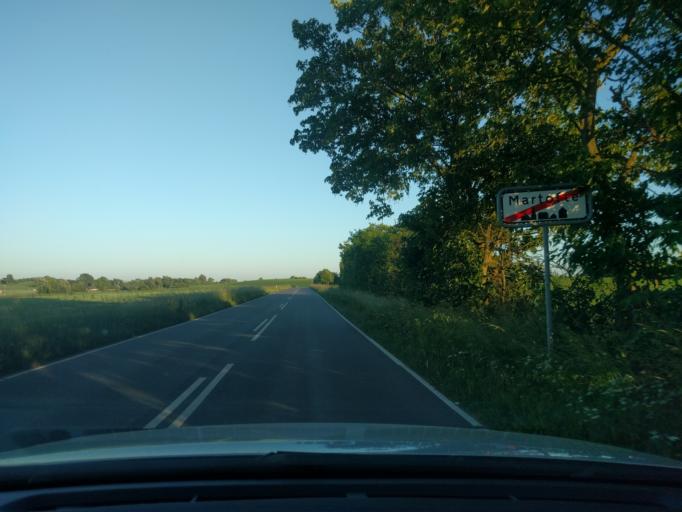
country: DK
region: South Denmark
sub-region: Kerteminde Kommune
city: Kerteminde
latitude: 55.5399
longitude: 10.6621
